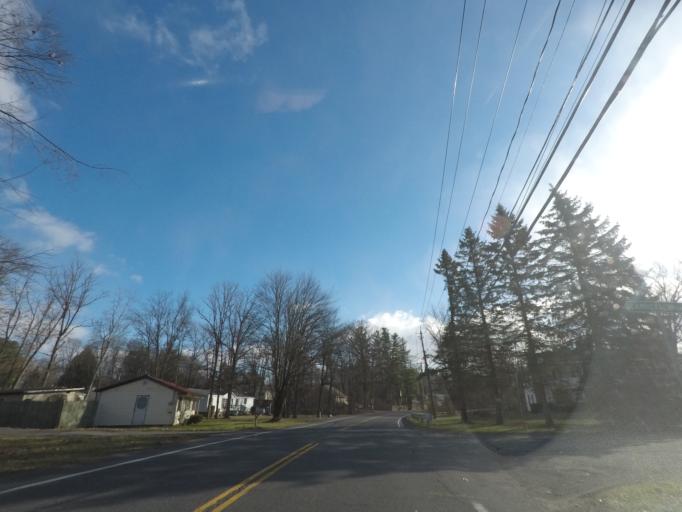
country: US
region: New York
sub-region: Schenectady County
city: Niskayuna
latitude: 42.7461
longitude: -73.8704
